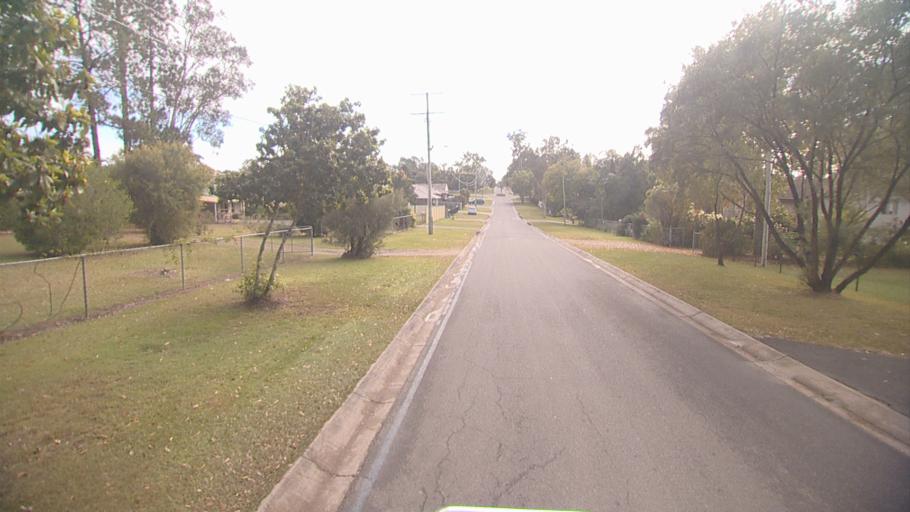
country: AU
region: Queensland
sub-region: Logan
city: Waterford West
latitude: -27.6845
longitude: 153.1245
